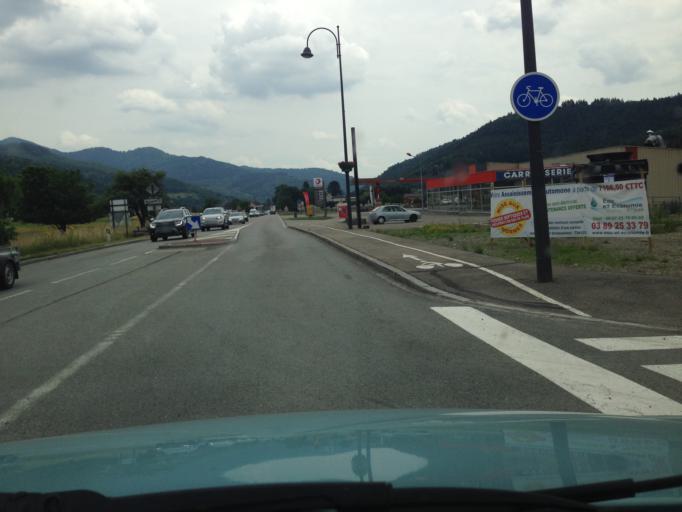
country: FR
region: Alsace
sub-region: Departement du Haut-Rhin
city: Moosch
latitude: 47.8564
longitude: 7.0540
